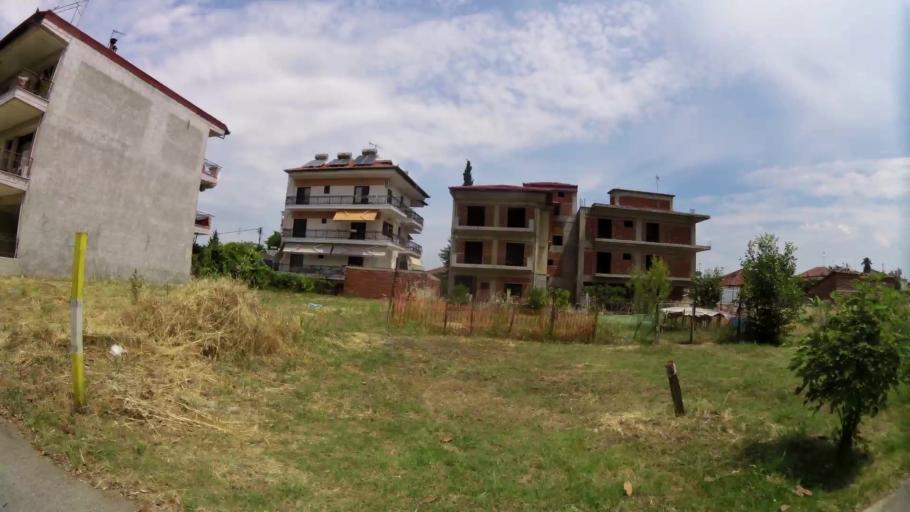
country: GR
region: Central Macedonia
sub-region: Nomos Pierias
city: Katerini
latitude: 40.2639
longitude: 22.5197
